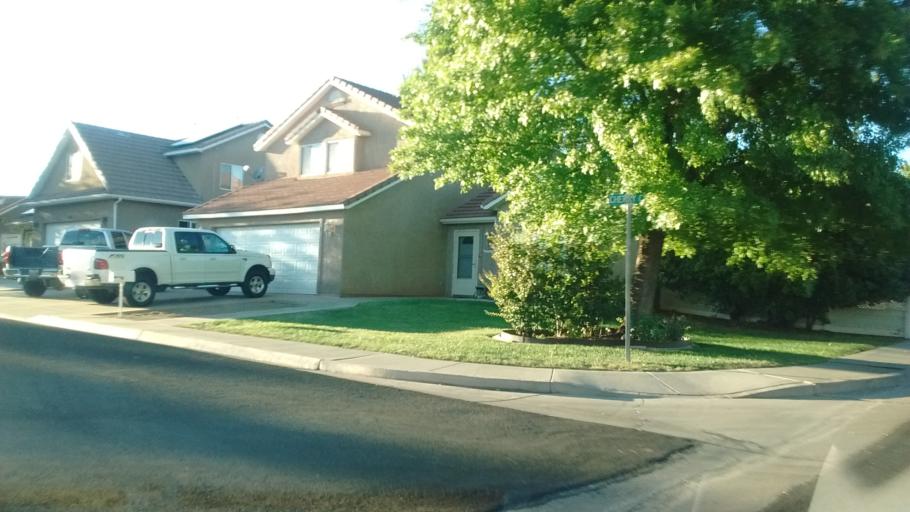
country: US
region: Utah
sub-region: Washington County
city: Washington
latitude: 37.1385
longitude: -113.4961
